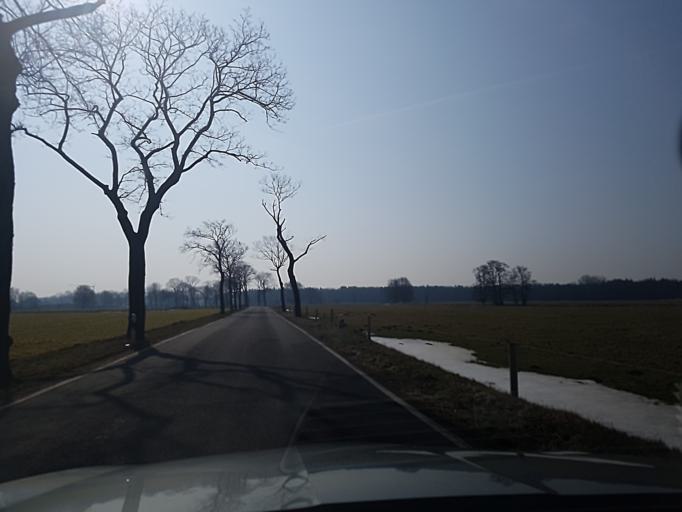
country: DE
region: Brandenburg
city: Falkenberg
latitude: 51.6401
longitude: 13.2696
